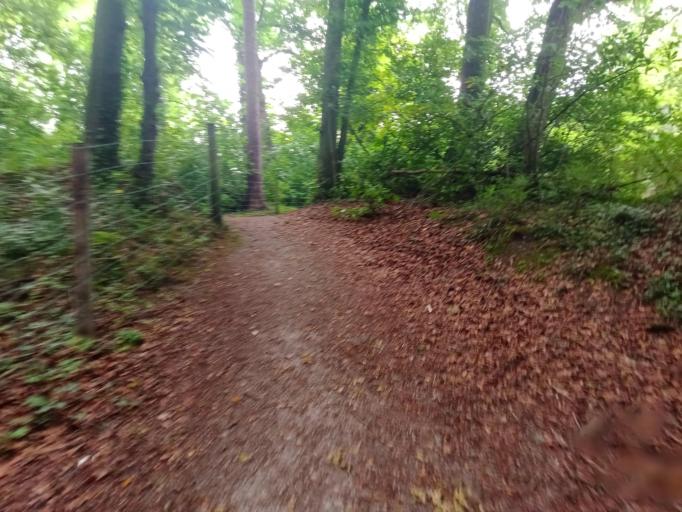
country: IE
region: Leinster
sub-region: Laois
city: Abbeyleix
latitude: 52.9096
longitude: -7.3572
